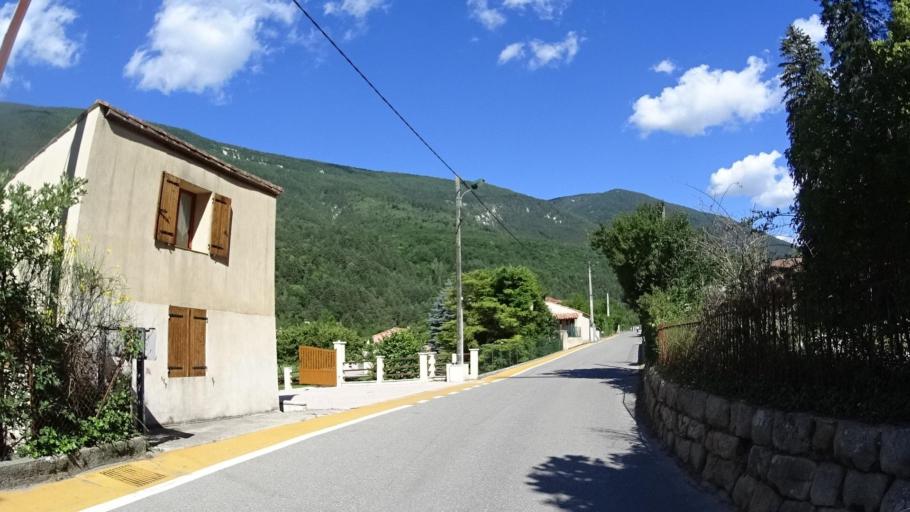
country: FR
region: Provence-Alpes-Cote d'Azur
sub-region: Departement des Alpes-de-Haute-Provence
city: Annot
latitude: 43.9723
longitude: 6.6573
